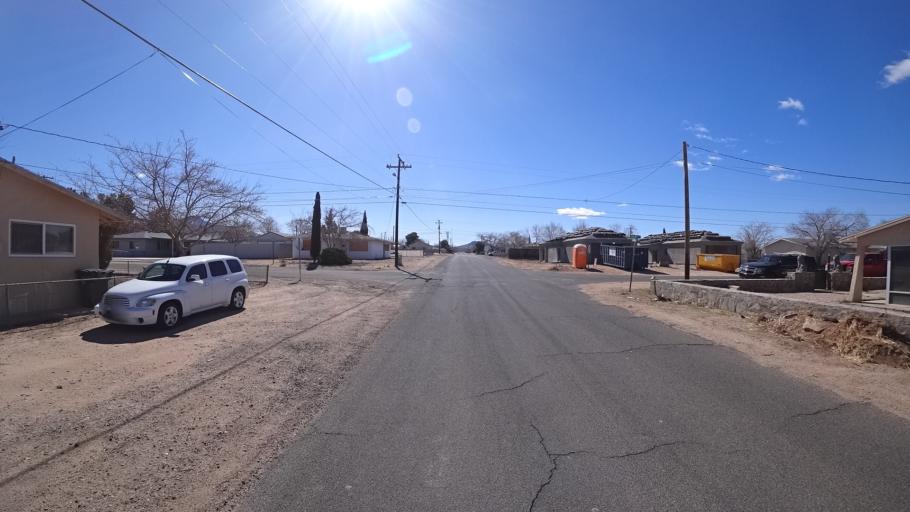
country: US
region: Arizona
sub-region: Mohave County
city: Kingman
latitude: 35.1974
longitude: -114.0202
